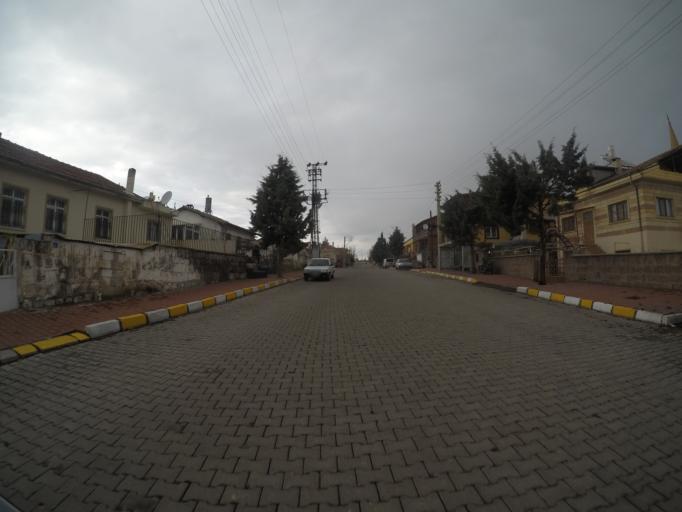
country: TR
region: Nevsehir
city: Goereme
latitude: 38.6291
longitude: 34.8588
